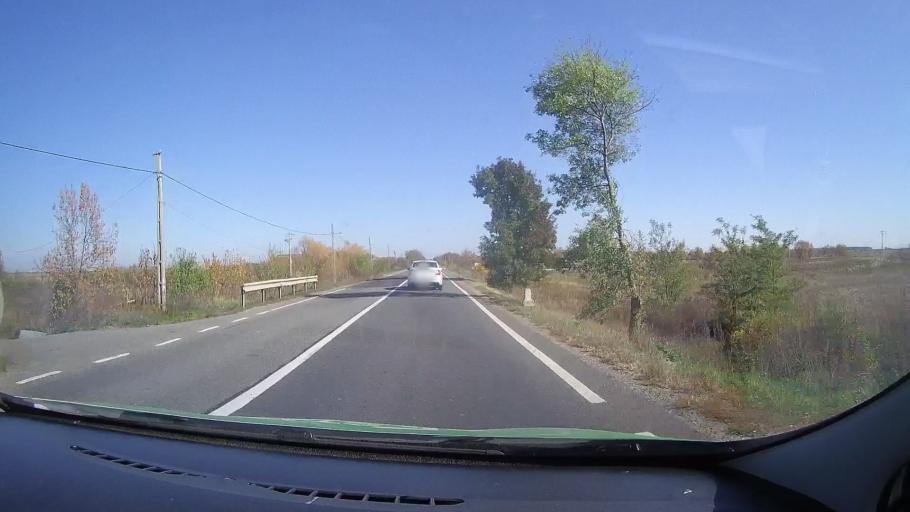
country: RO
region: Satu Mare
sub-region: Comuna Doba
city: Doba
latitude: 47.7226
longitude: 22.6671
